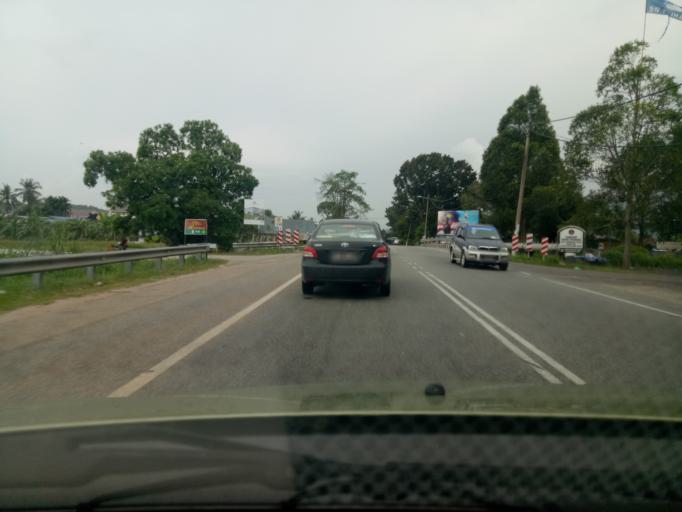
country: MY
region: Kedah
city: Gurun
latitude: 5.8678
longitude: 100.4537
